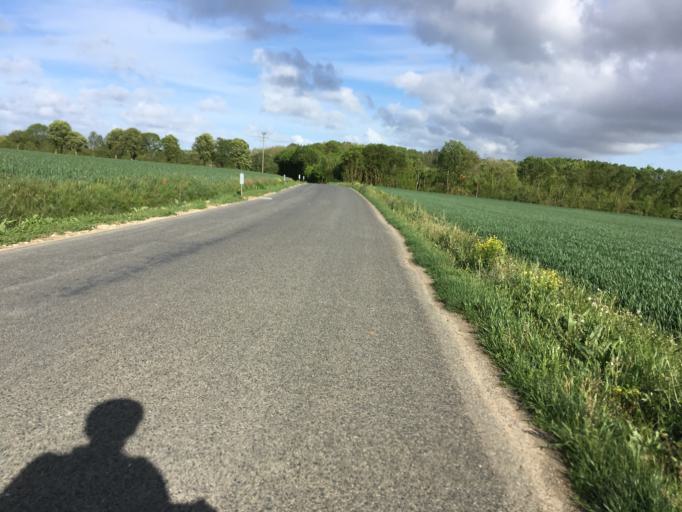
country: FR
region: Poitou-Charentes
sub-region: Departement de la Charente-Maritime
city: Verines
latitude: 46.1784
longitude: -0.9279
